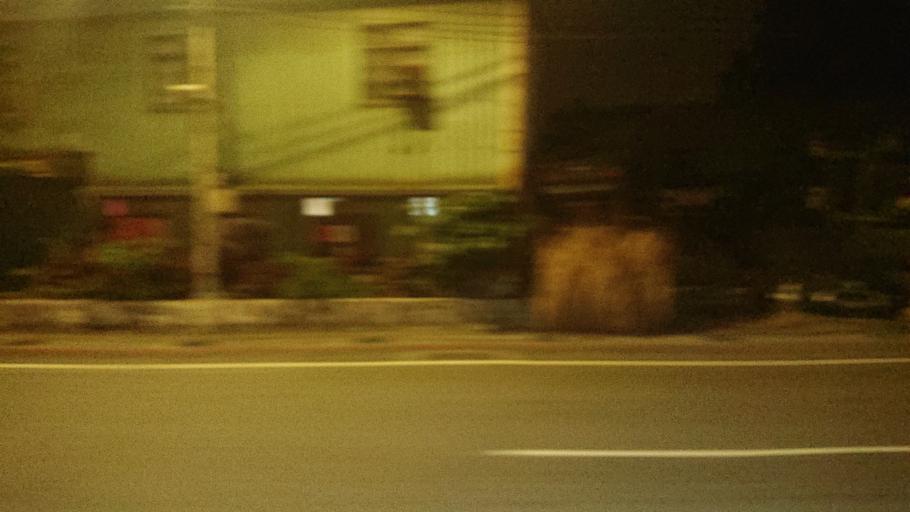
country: TW
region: Taipei
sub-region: Taipei
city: Banqiao
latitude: 24.9472
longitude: 121.4063
